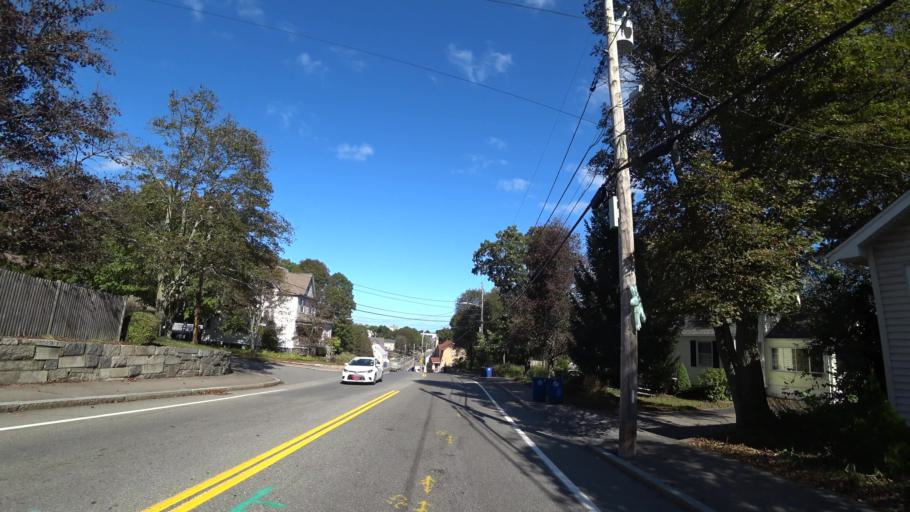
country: US
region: Massachusetts
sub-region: Norfolk County
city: Braintree
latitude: 42.2301
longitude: -70.9816
